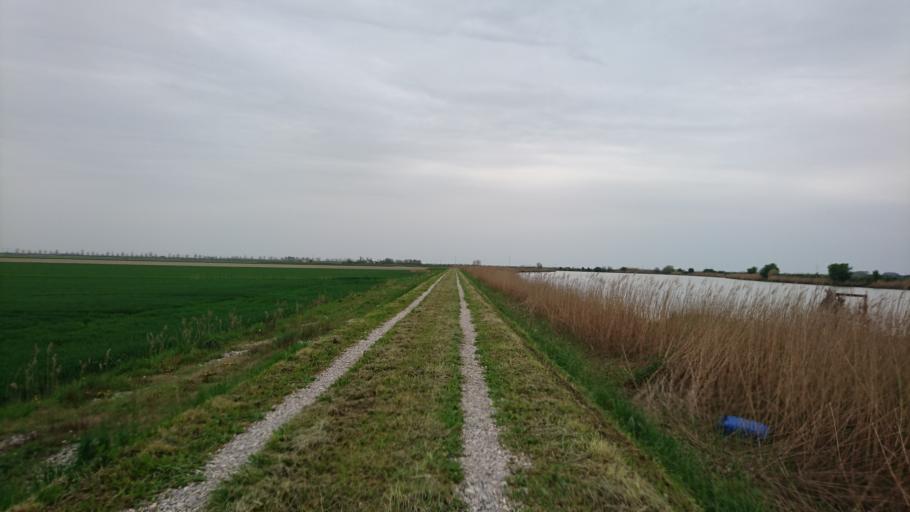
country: IT
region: Veneto
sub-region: Provincia di Venezia
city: Lugugnana
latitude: 45.6797
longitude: 12.9524
